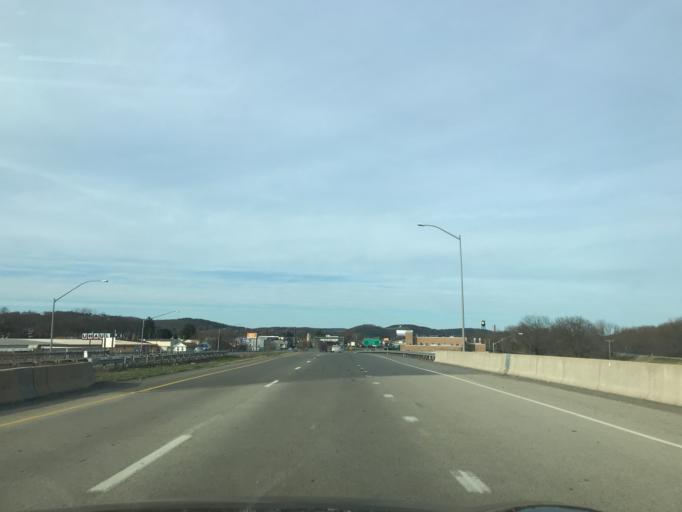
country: US
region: Pennsylvania
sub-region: Lycoming County
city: Williamsport
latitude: 41.2415
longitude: -76.9949
